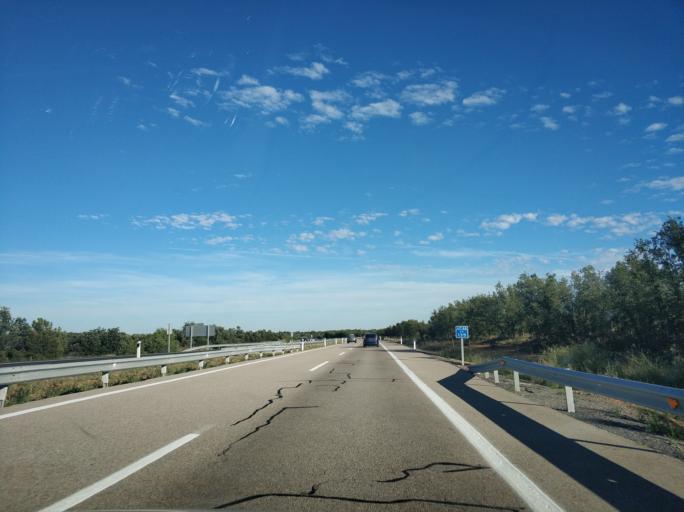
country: ES
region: Castille and Leon
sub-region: Provincia de Leon
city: Valverde de la Virgen
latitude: 42.6118
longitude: -5.7303
